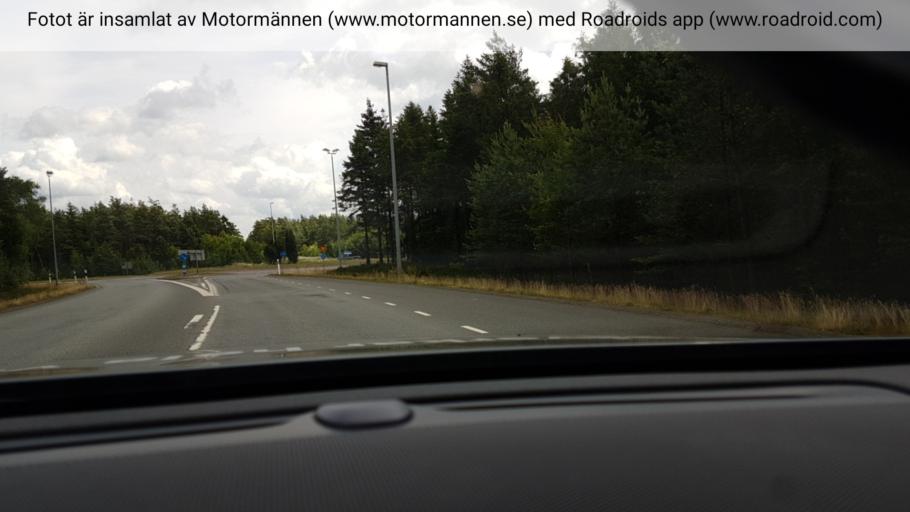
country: SE
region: Skane
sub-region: Hassleholms Kommun
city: Hassleholm
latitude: 56.1696
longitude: 13.8324
